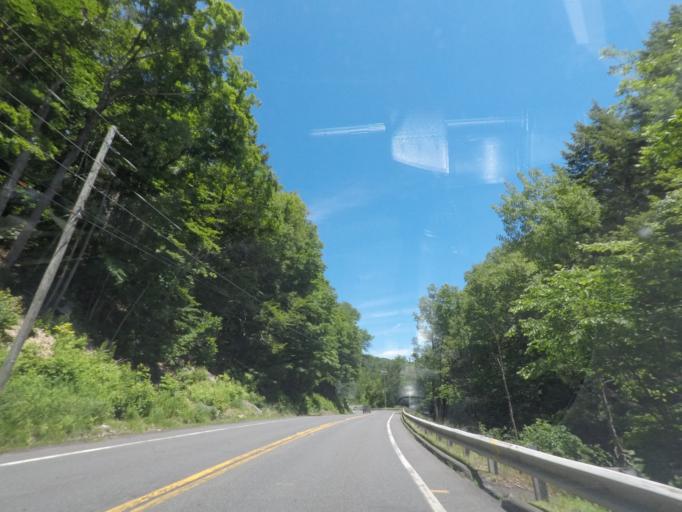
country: US
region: Massachusetts
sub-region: Berkshire County
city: Becket
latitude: 42.2695
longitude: -73.0242
